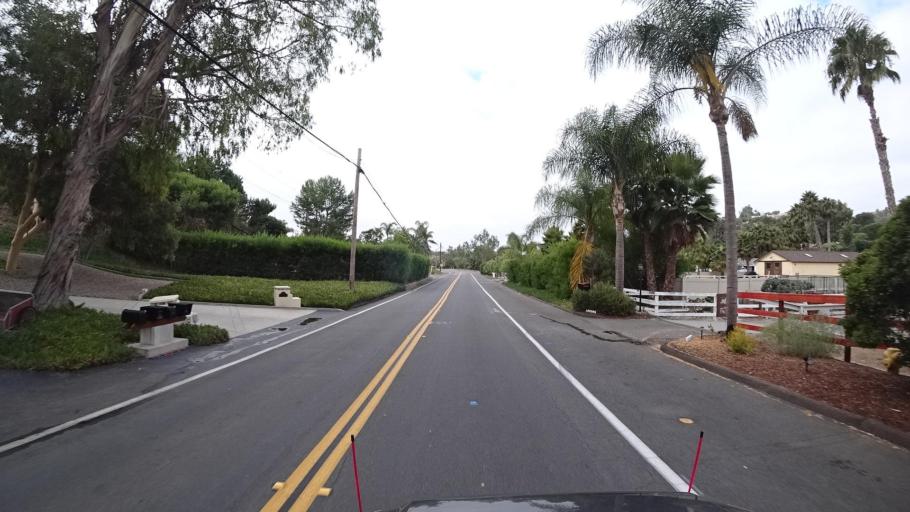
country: US
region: California
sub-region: San Diego County
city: Fairbanks Ranch
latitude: 32.9858
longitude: -117.2258
